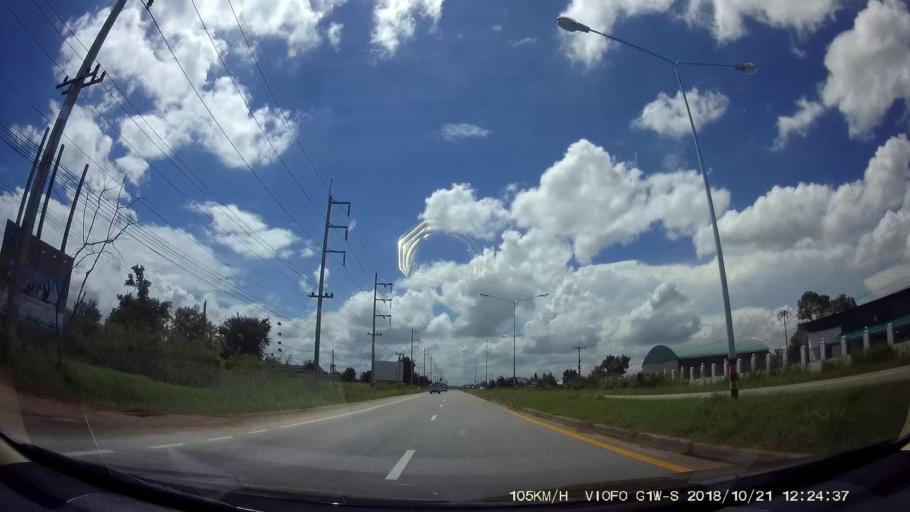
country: TH
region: Nakhon Ratchasima
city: Dan Khun Thot
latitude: 15.2312
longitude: 101.7812
